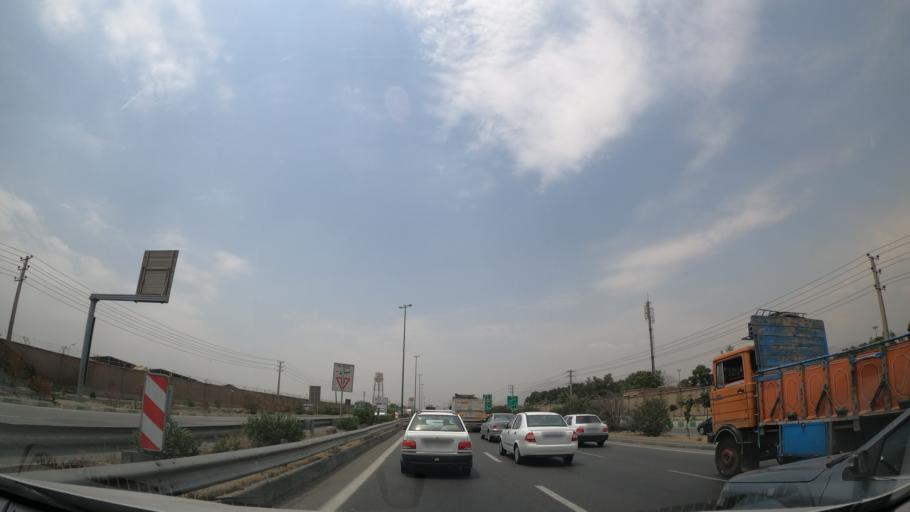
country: IR
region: Tehran
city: Shahr-e Qods
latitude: 35.6905
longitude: 51.2156
